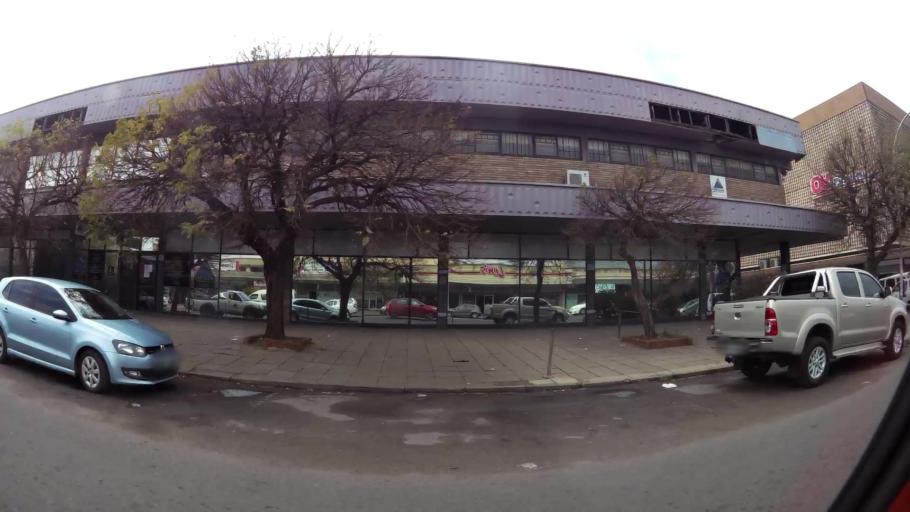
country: ZA
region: Gauteng
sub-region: Sedibeng District Municipality
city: Vanderbijlpark
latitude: -26.6969
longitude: 27.8354
